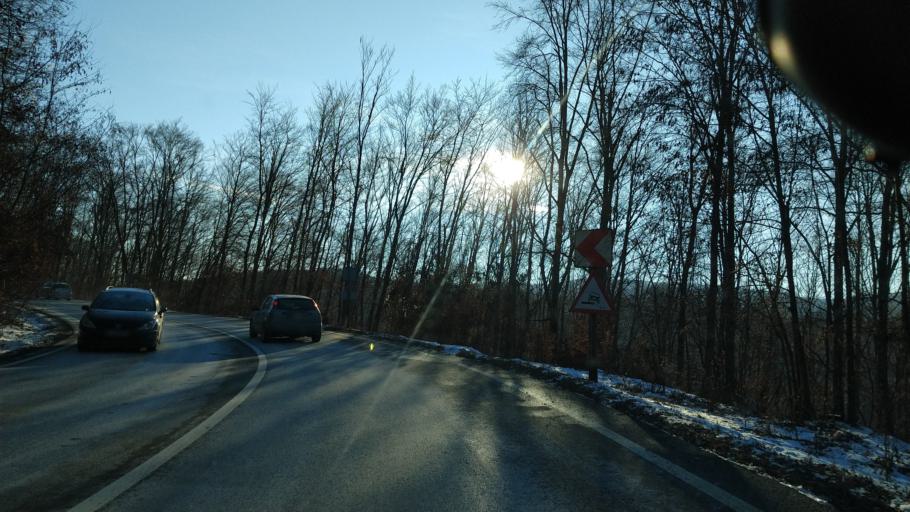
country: RO
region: Bacau
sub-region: Comuna Luizi-Calugara
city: Luizi-Calugara
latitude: 46.5378
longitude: 26.8203
